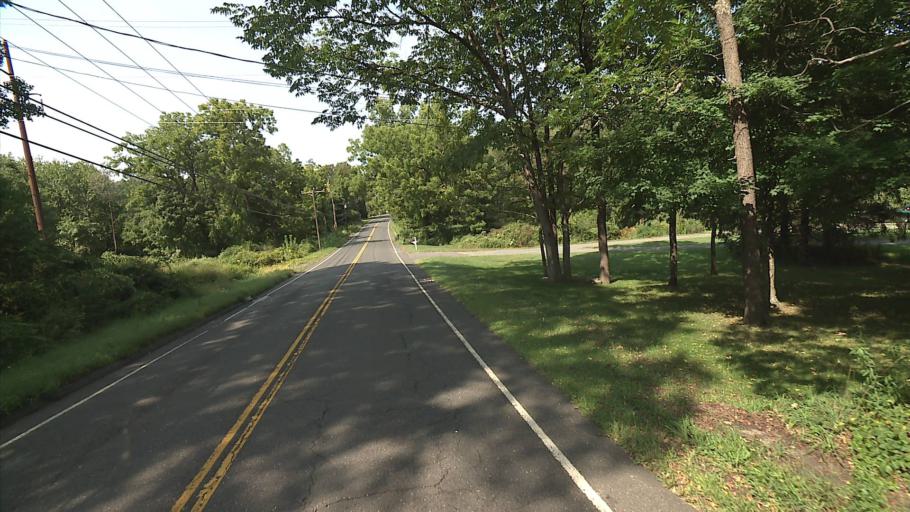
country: US
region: Connecticut
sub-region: New Haven County
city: Heritage Village
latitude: 41.4808
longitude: -73.2569
